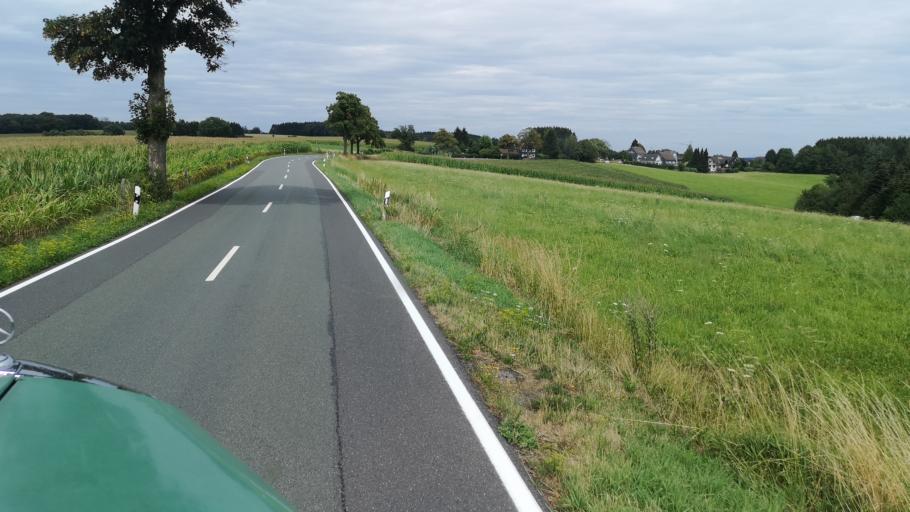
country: DE
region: North Rhine-Westphalia
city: Wermelskirchen
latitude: 51.1302
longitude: 7.2658
